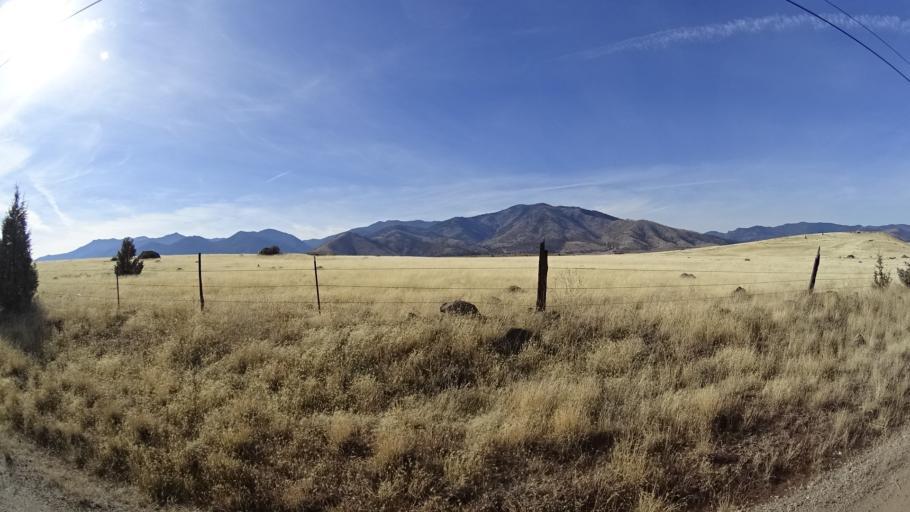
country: US
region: California
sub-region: Siskiyou County
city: Weed
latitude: 41.4909
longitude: -122.4510
